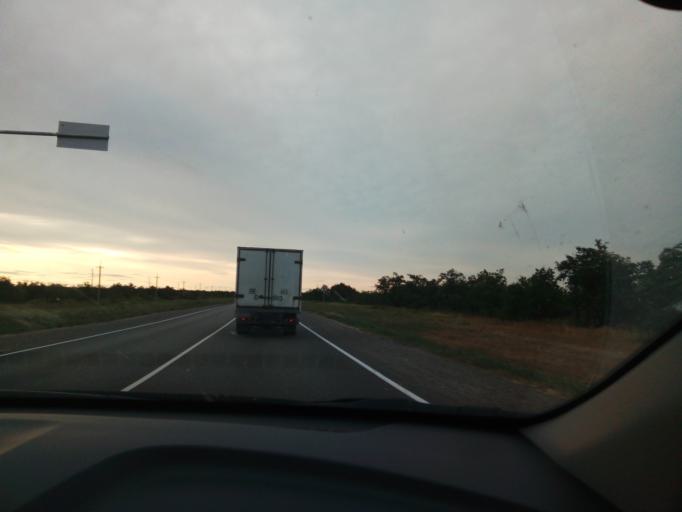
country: RU
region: Volgograd
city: Primorsk
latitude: 49.2228
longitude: 44.9058
